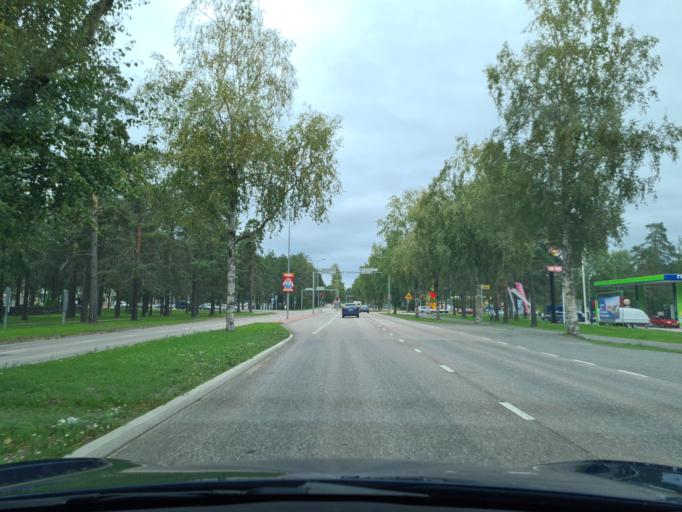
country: FI
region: South Karelia
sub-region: Lappeenranta
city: Lappeenranta
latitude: 61.0439
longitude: 28.1785
